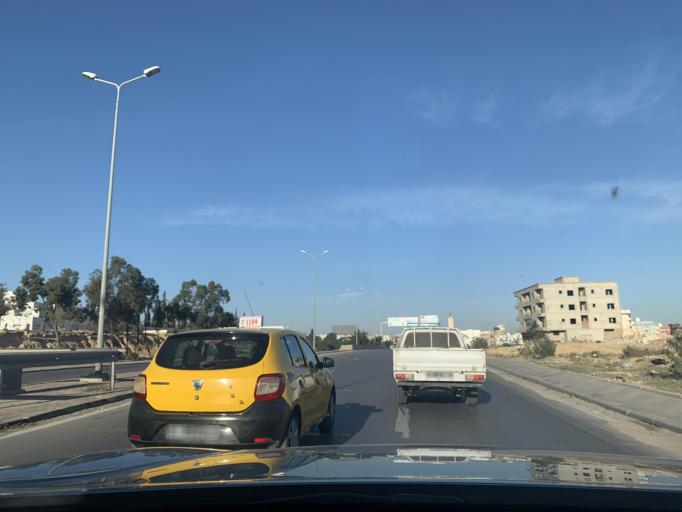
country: DZ
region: Souk Ahras
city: Souk Ahras
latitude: 36.3645
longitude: 8.0051
